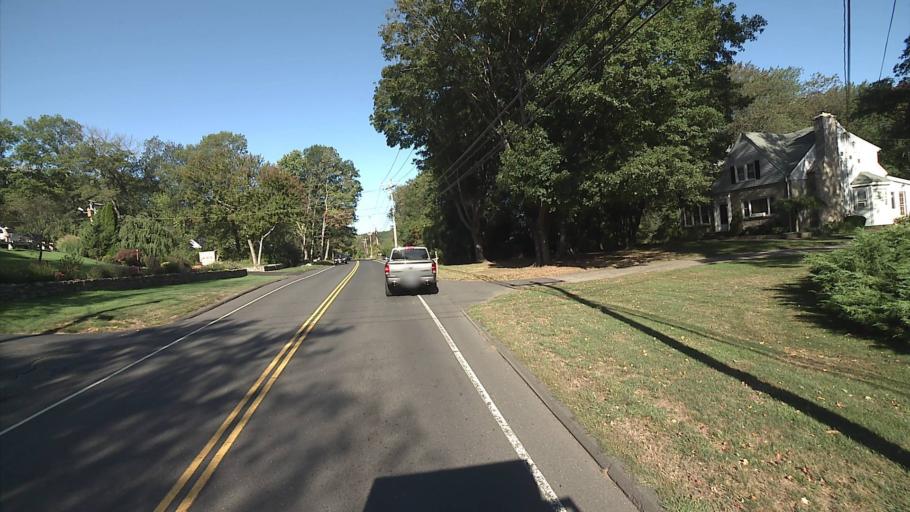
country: US
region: Connecticut
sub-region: New Haven County
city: Prospect
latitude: 41.4991
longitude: -72.9611
